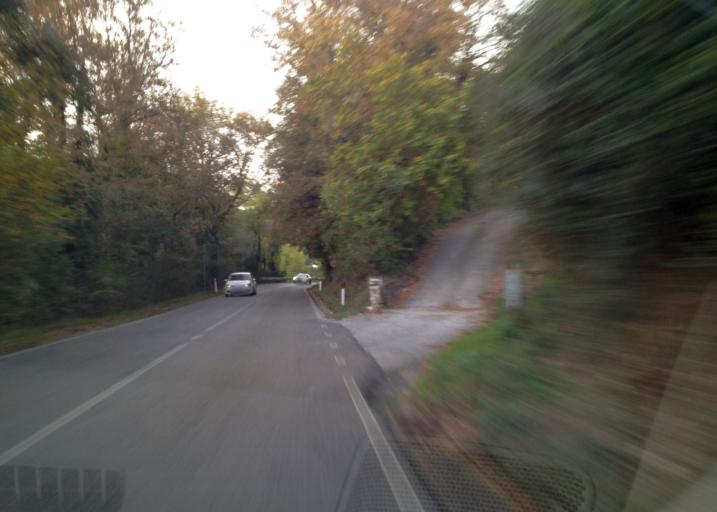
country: IT
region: Tuscany
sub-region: Province of Florence
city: Panzano in Chianti
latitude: 43.5144
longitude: 11.2913
